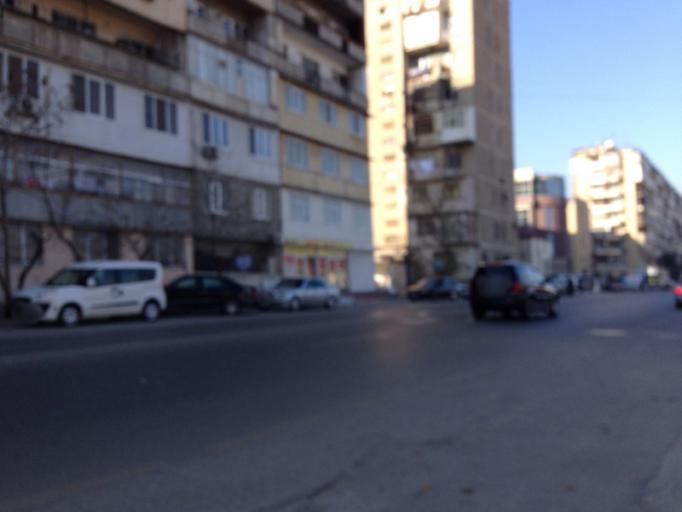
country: AZ
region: Baki
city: Baku
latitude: 40.4075
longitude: 49.8748
